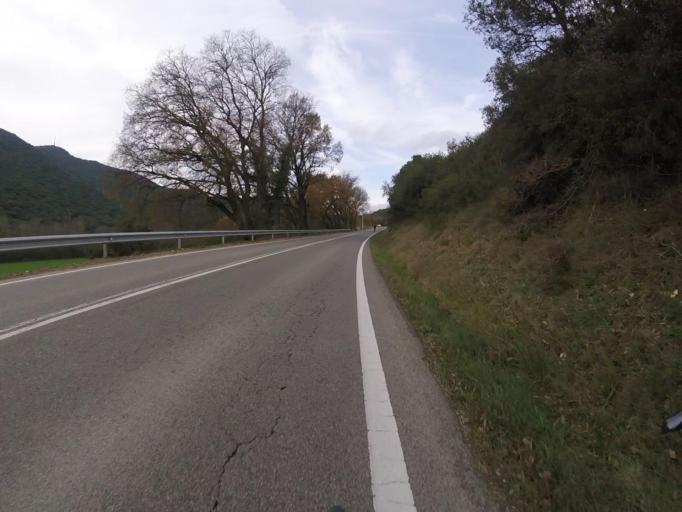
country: ES
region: Navarre
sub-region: Provincia de Navarra
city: Estella
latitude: 42.6977
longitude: -2.0536
